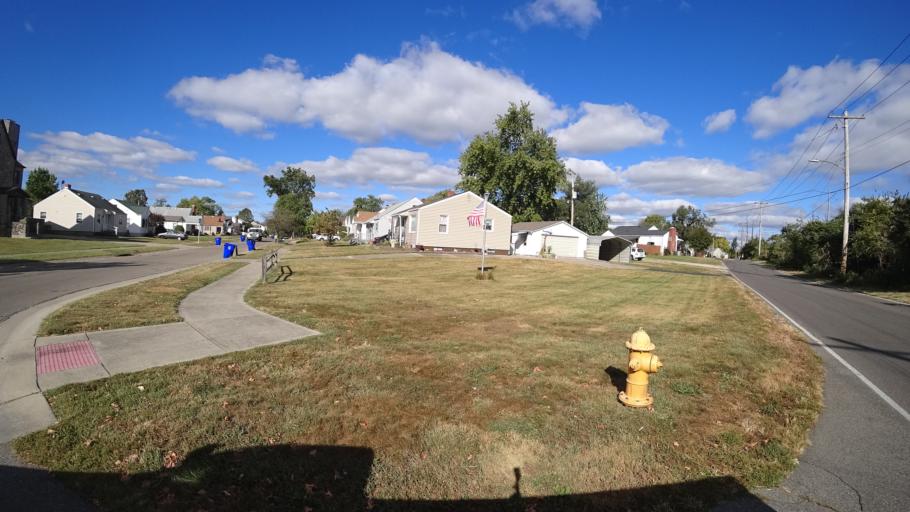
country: US
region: Ohio
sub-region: Butler County
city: Fairfield
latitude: 39.3651
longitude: -84.5483
